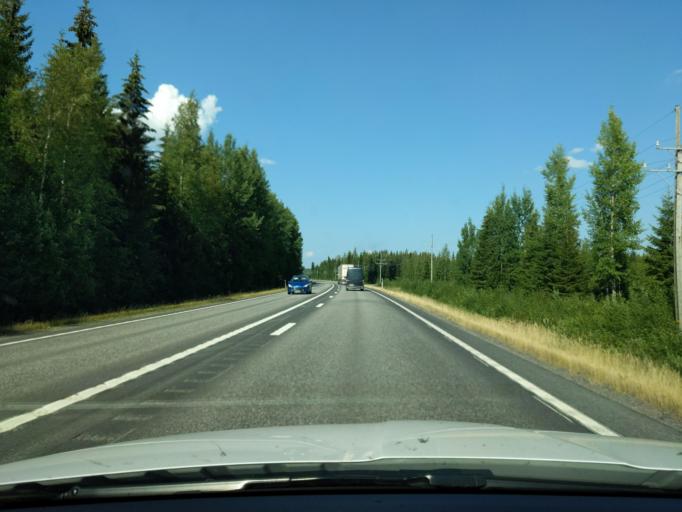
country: FI
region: Paijanne Tavastia
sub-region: Lahti
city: Jaervelae
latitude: 60.9151
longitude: 25.3526
